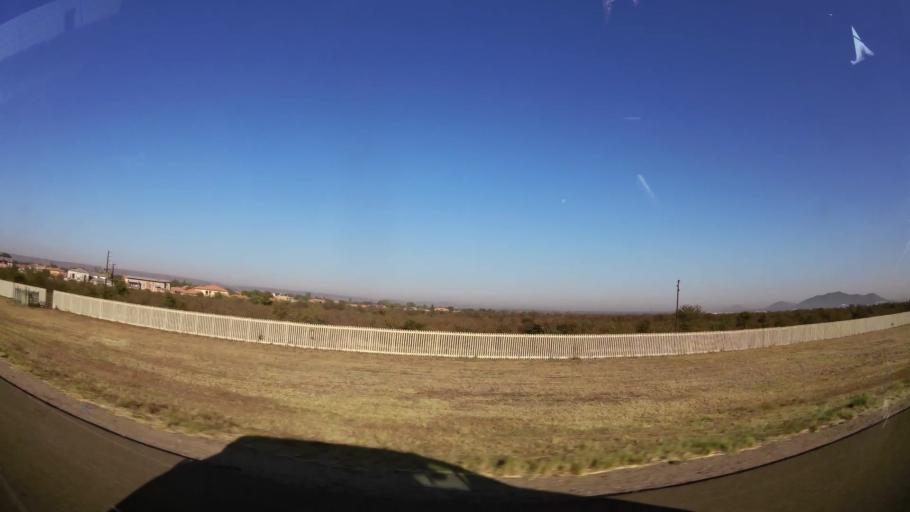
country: ZA
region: Gauteng
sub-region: City of Tshwane Metropolitan Municipality
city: Pretoria
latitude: -25.6481
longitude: 28.2735
